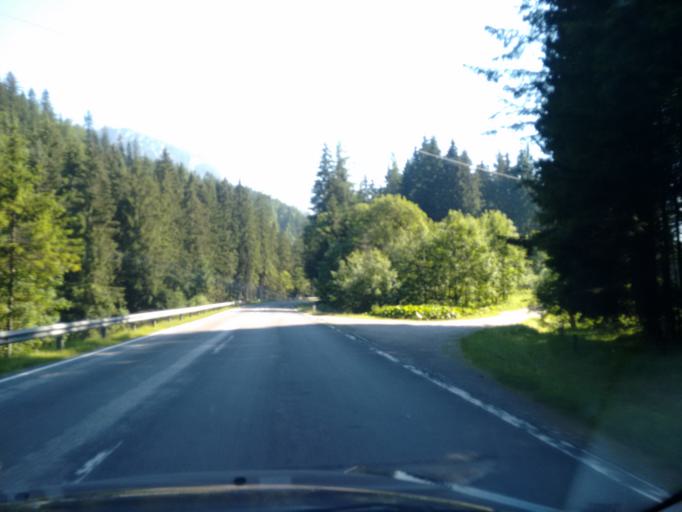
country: AT
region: Styria
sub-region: Politischer Bezirk Liezen
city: Altaussee
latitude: 47.6264
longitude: 13.7044
